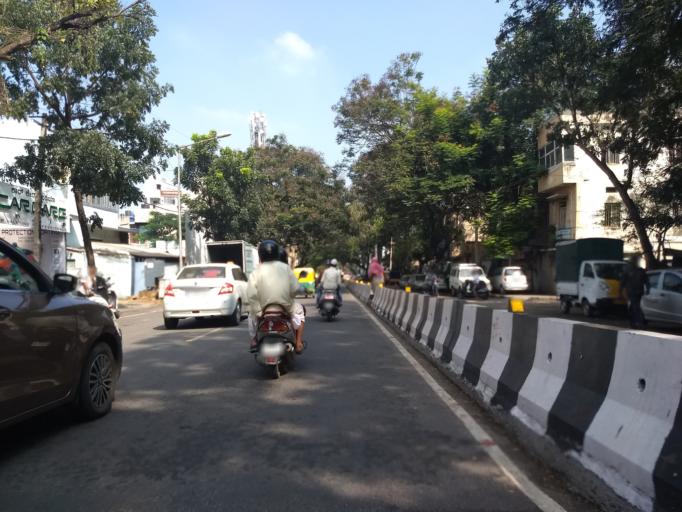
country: IN
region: Karnataka
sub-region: Bangalore Urban
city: Bangalore
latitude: 12.9517
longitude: 77.5799
